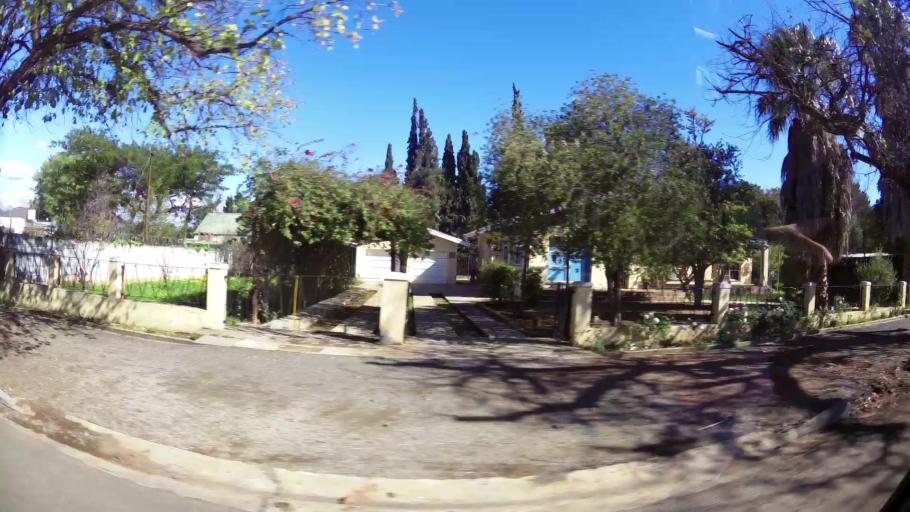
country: ZA
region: Western Cape
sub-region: Cape Winelands District Municipality
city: Ashton
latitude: -33.8003
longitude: 19.8812
